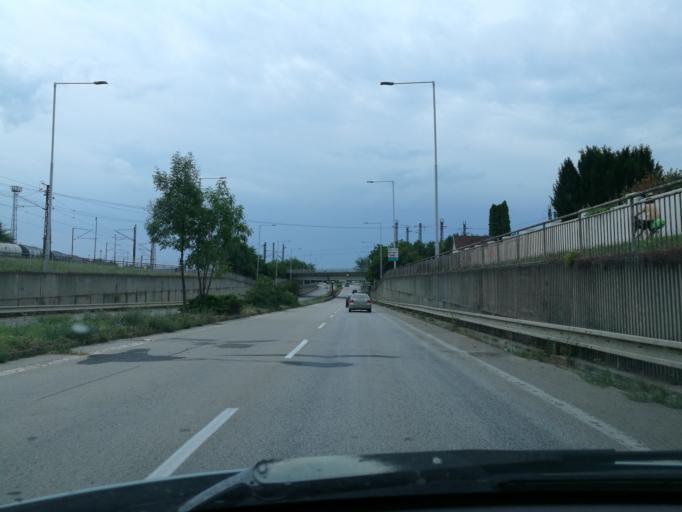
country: SK
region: Nitriansky
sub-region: Okres Nove Zamky
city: Nove Zamky
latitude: 48.0068
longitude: 18.1565
